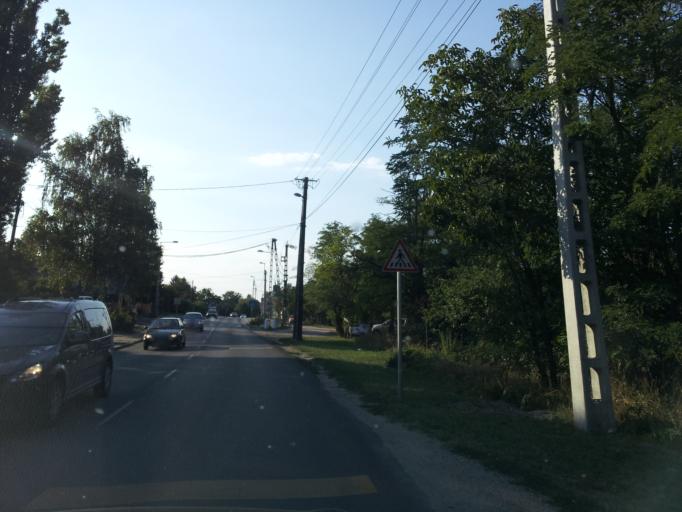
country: HU
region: Pest
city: Tahitotfalu
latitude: 47.7417
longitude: 19.0856
